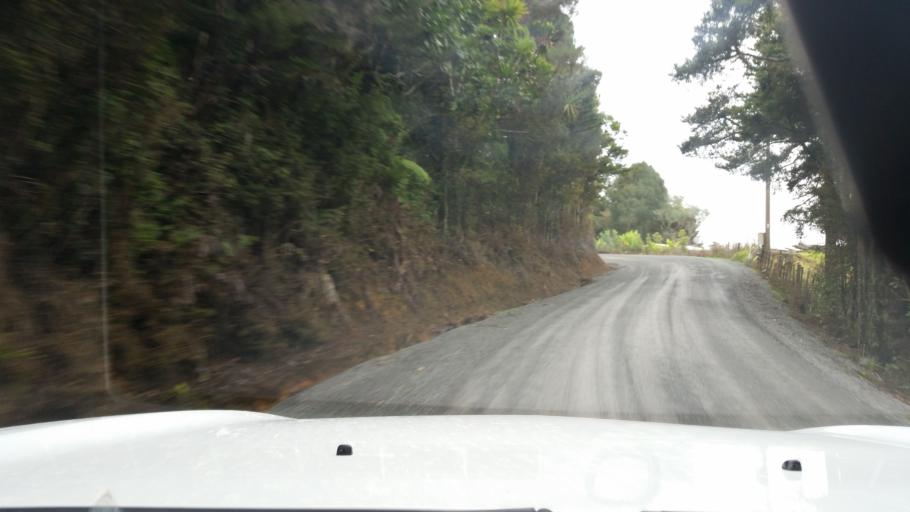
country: NZ
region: Northland
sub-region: Whangarei
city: Whangarei
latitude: -35.7337
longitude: 174.4312
